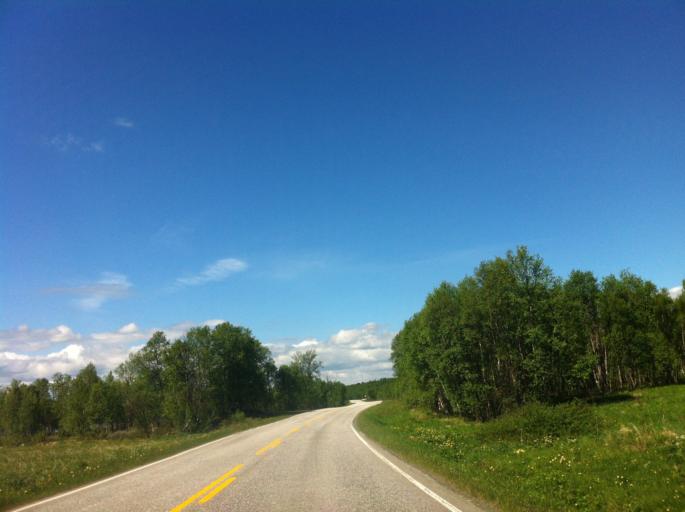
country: NO
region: Sor-Trondelag
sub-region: Roros
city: Roros
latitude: 62.5997
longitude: 11.5009
